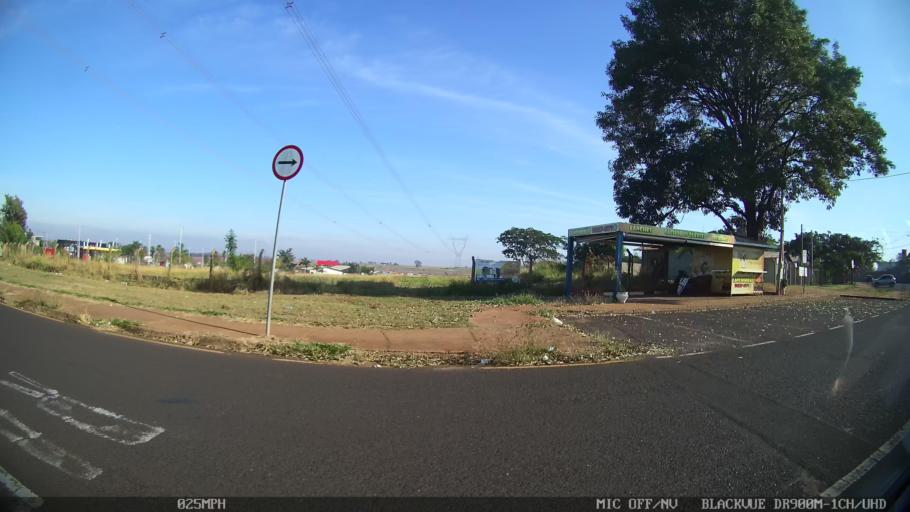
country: BR
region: Sao Paulo
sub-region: Sao Jose Do Rio Preto
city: Sao Jose do Rio Preto
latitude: -20.7690
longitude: -49.3282
